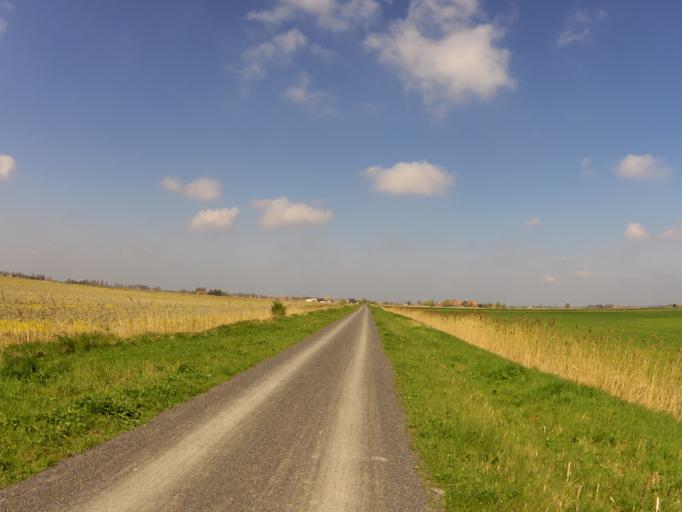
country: BE
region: Flanders
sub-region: Provincie West-Vlaanderen
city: Diksmuide
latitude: 51.0581
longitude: 2.8150
